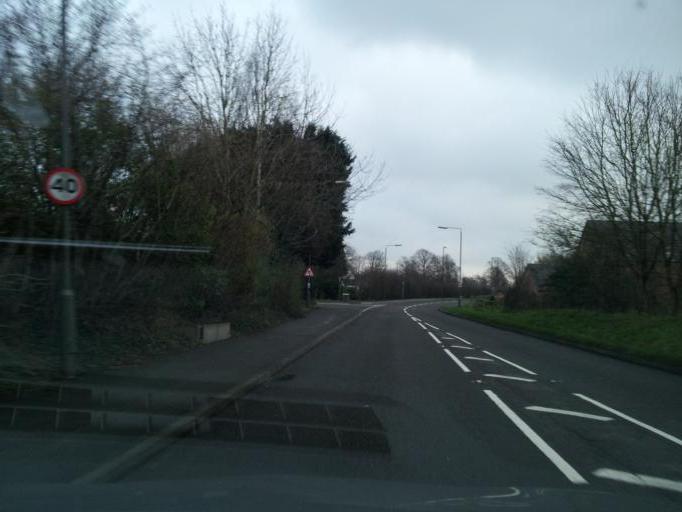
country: GB
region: England
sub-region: Derbyshire
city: Etwall
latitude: 52.8712
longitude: -1.6240
